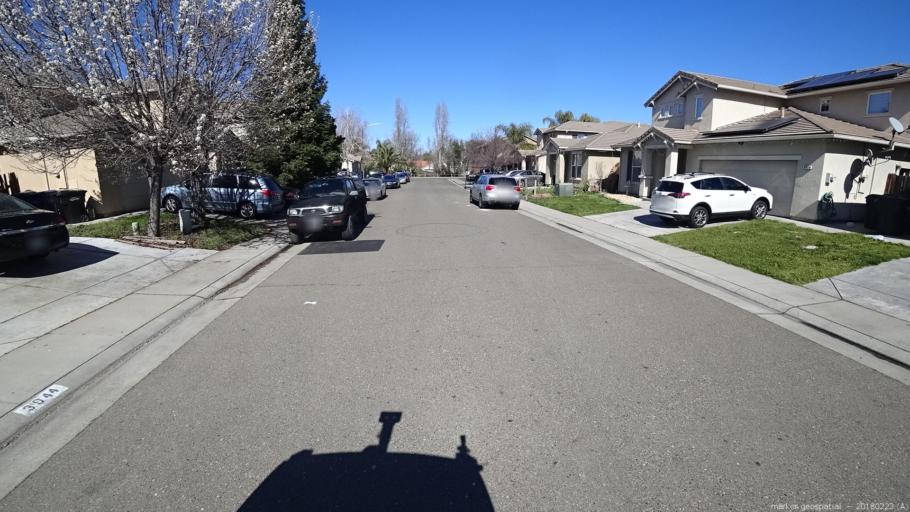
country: US
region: California
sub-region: Sacramento County
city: North Highlands
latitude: 38.7132
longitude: -121.3730
